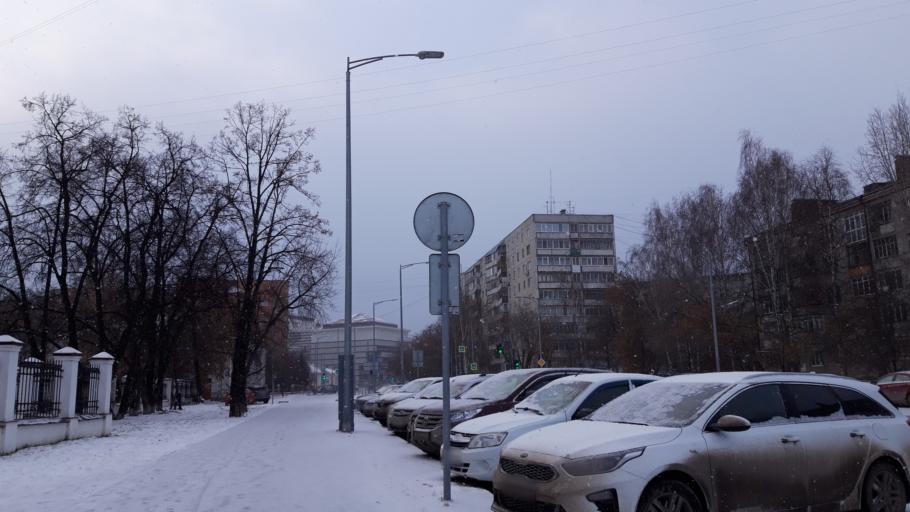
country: RU
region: Tjumen
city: Tyumen
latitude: 57.1569
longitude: 65.5513
